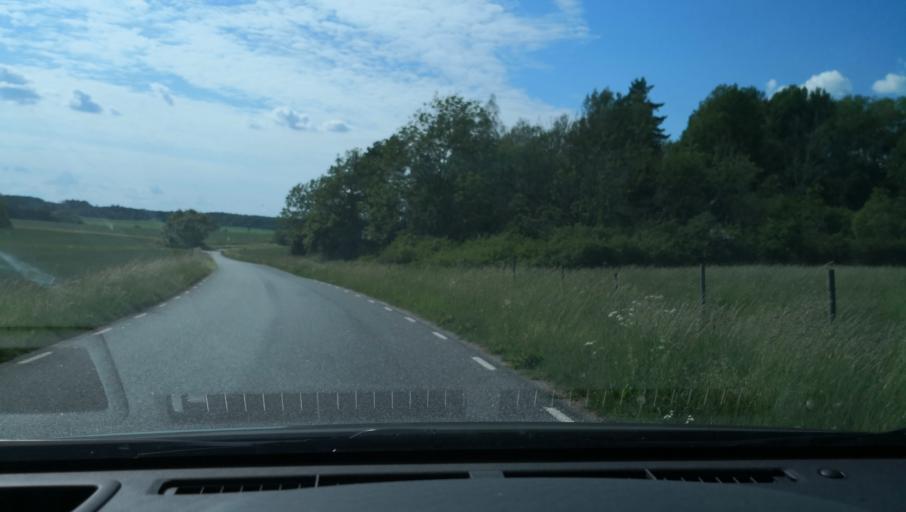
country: SE
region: Uppsala
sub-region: Enkopings Kommun
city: Orsundsbro
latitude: 59.8350
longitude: 17.3122
